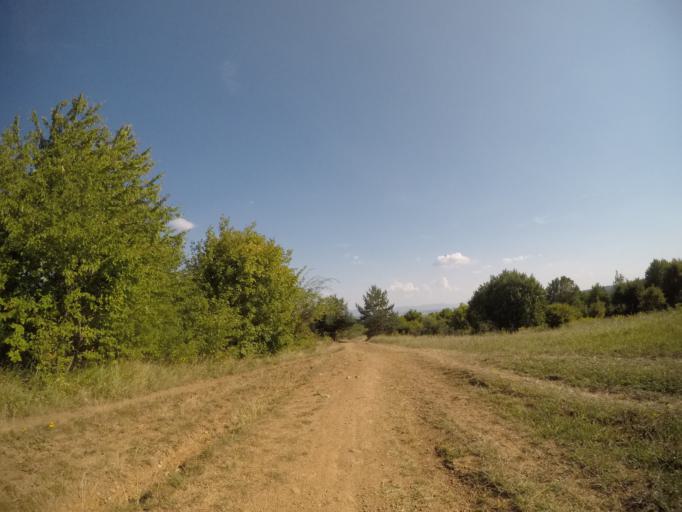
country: SK
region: Kosicky
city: Kosice
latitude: 48.7390
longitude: 21.2096
